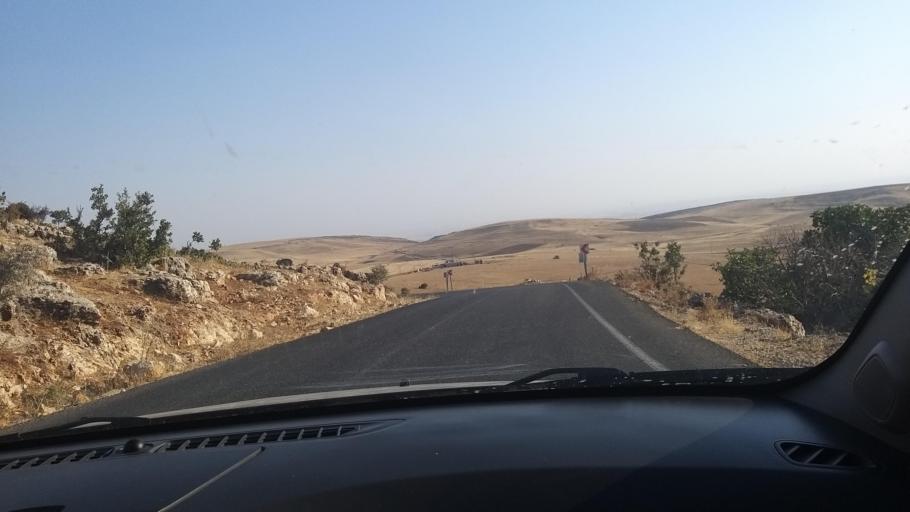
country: TR
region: Diyarbakir
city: Silvan
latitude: 38.1910
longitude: 41.0074
